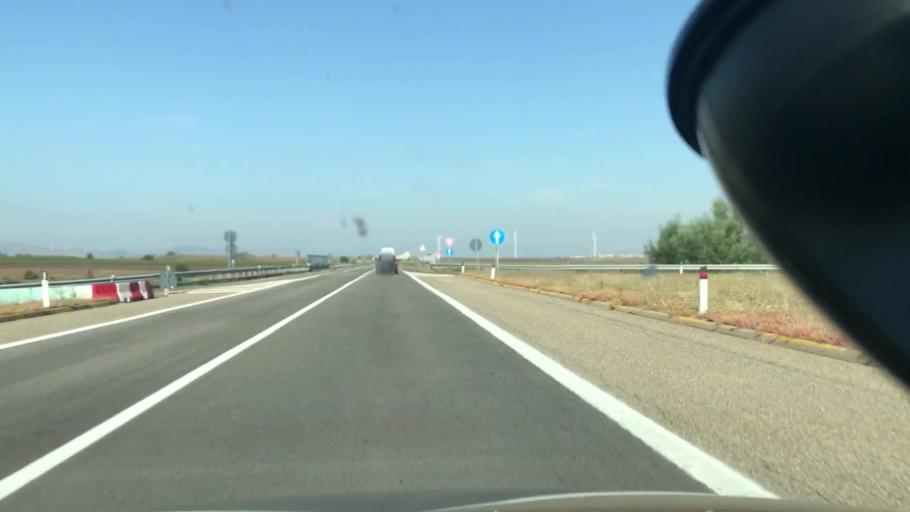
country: IT
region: Basilicate
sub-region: Provincia di Potenza
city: Venosa
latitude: 41.0089
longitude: 15.8409
